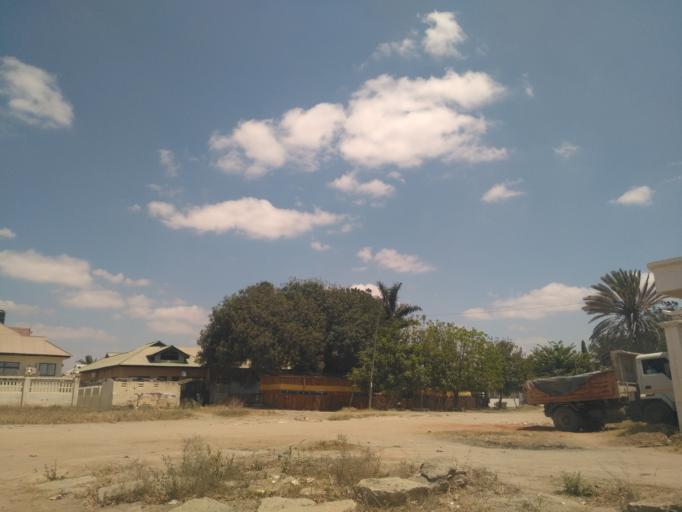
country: TZ
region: Dodoma
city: Dodoma
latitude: -6.1740
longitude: 35.7536
